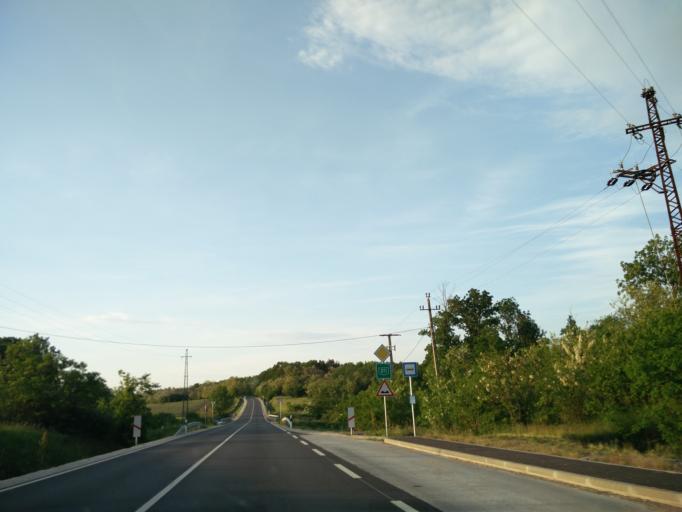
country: HU
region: Fejer
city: Lovasbereny
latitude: 47.2672
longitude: 18.5258
